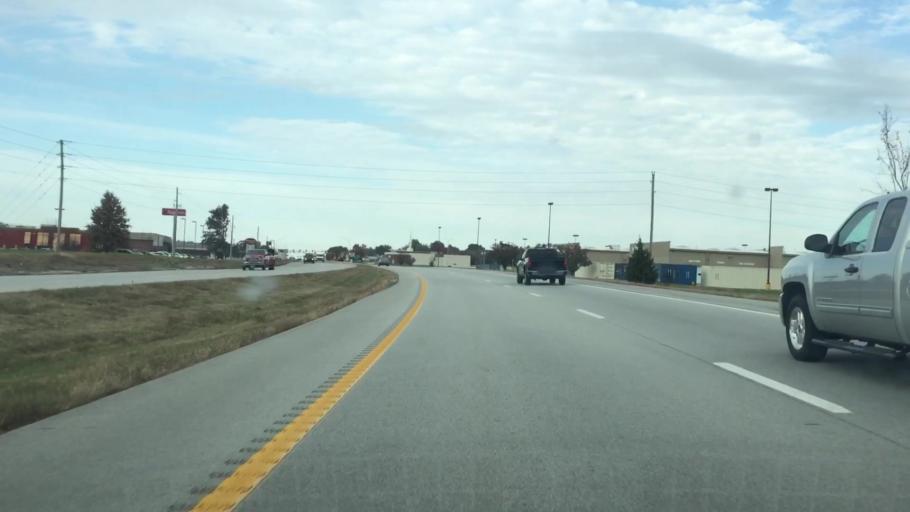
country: US
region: Missouri
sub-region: Henry County
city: Clinton
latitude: 38.3612
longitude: -93.7523
